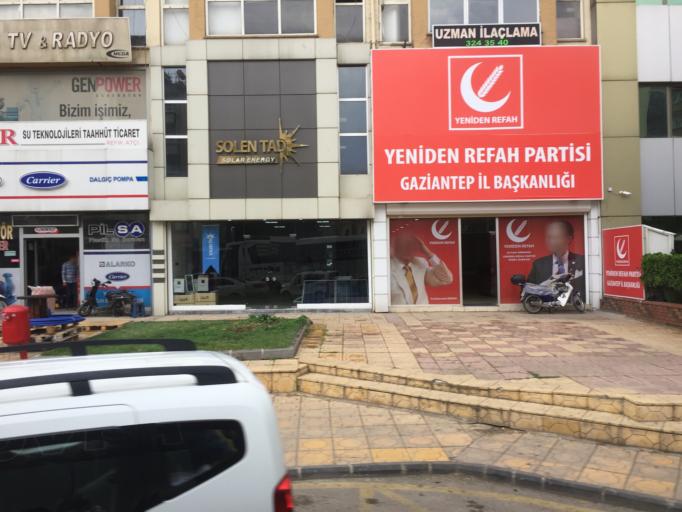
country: TR
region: Gaziantep
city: Gaziantep
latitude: 37.0713
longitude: 37.3721
